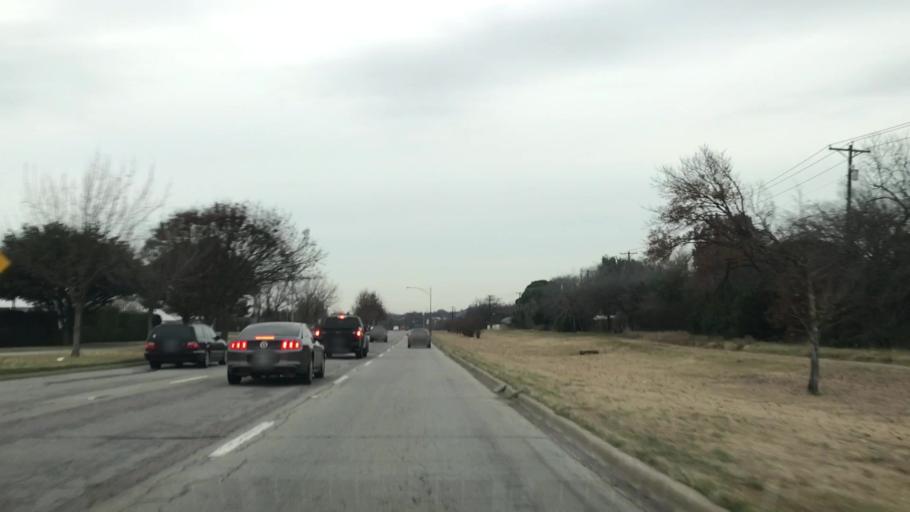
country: US
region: Texas
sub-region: Dallas County
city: University Park
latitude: 32.8537
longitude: -96.8445
